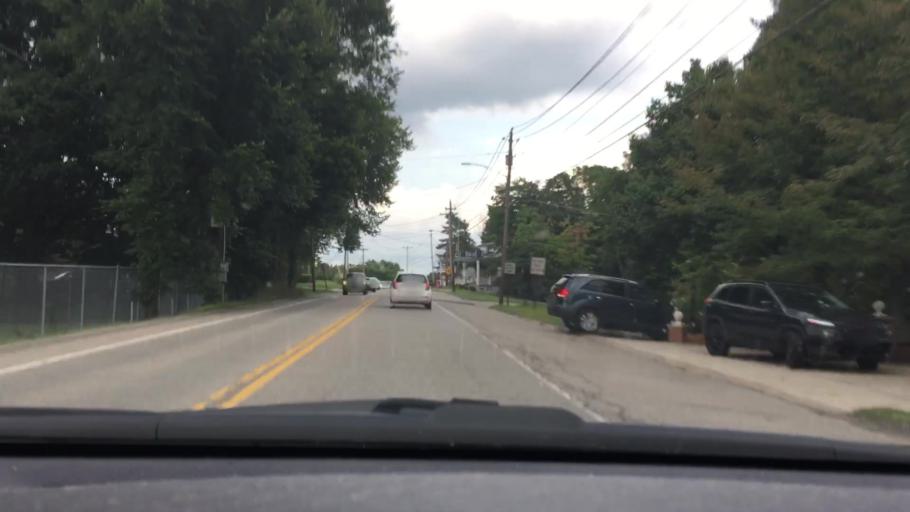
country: US
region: Pennsylvania
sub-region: Allegheny County
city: Bethel Park
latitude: 40.3442
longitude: -80.0322
